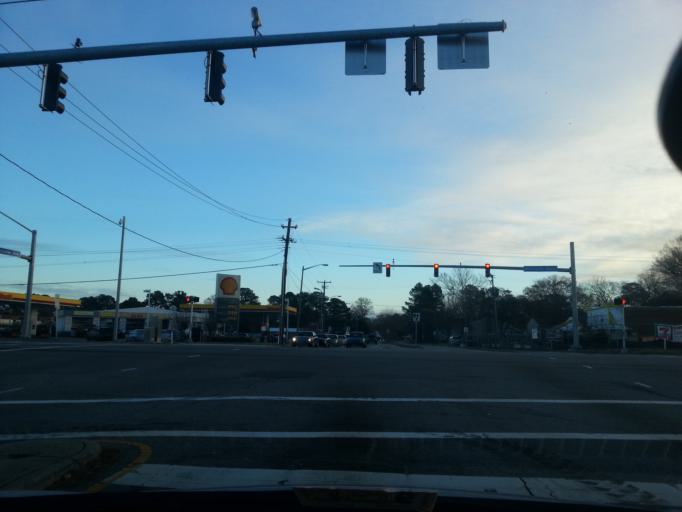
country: US
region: Virginia
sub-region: City of Norfolk
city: Norfolk
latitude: 36.8945
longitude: -76.2237
